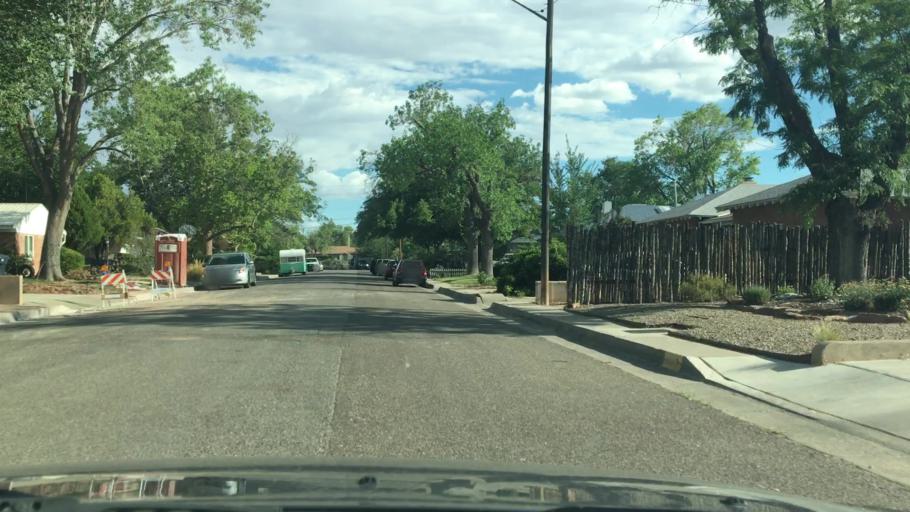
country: US
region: New Mexico
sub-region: Bernalillo County
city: Albuquerque
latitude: 35.0893
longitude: -106.6034
